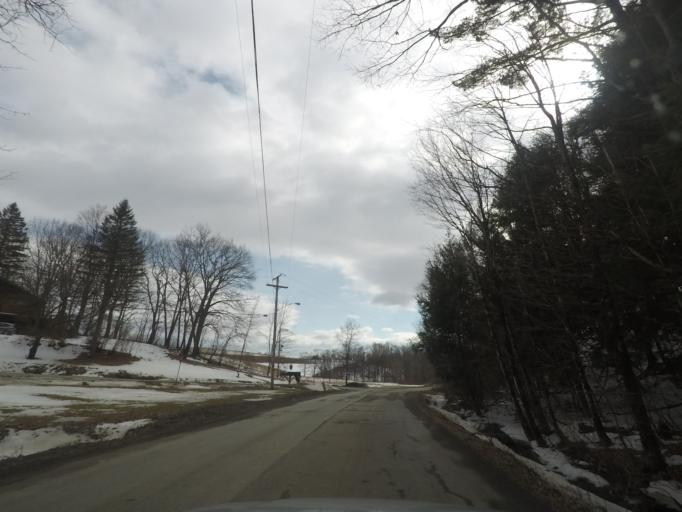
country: US
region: New York
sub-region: Saratoga County
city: Waterford
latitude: 42.7697
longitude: -73.6108
